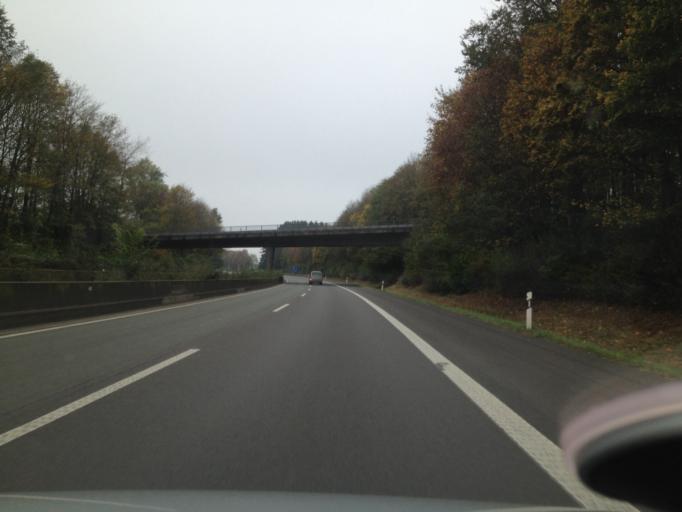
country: DE
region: North Rhine-Westphalia
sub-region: Regierungsbezirk Arnsberg
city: Drolshagen
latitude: 50.9739
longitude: 7.7328
